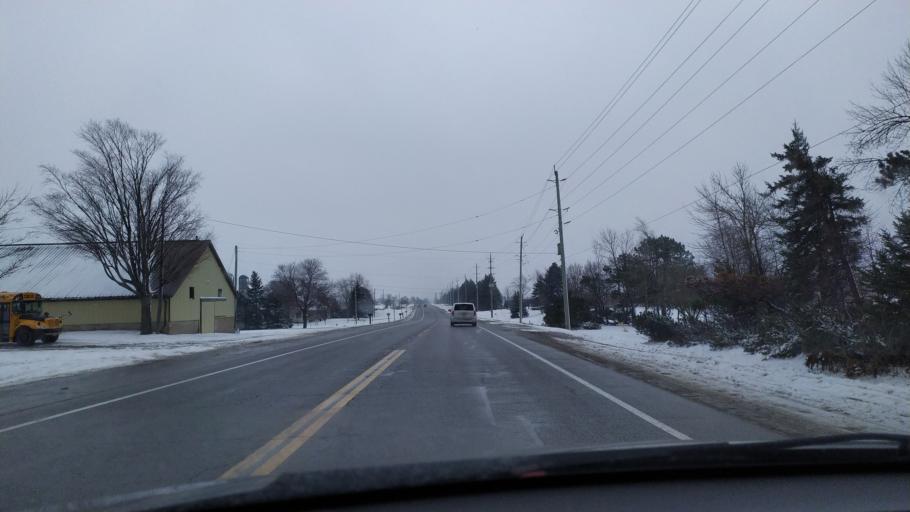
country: CA
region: Ontario
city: Waterloo
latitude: 43.6221
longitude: -80.6909
